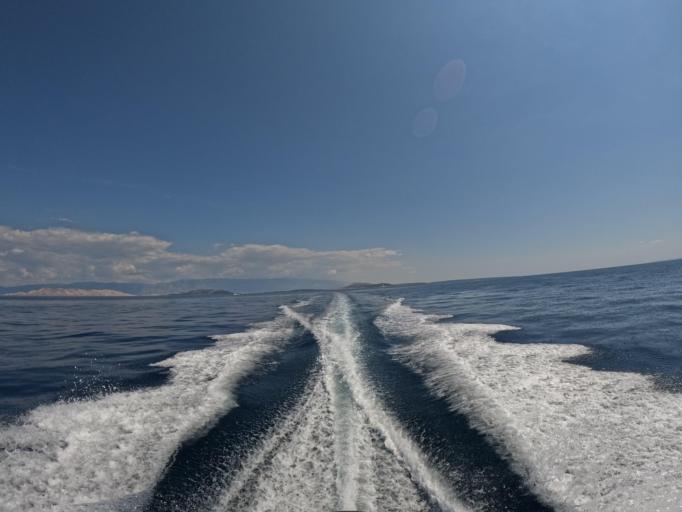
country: HR
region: Primorsko-Goranska
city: Punat
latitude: 44.8982
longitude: 14.6167
